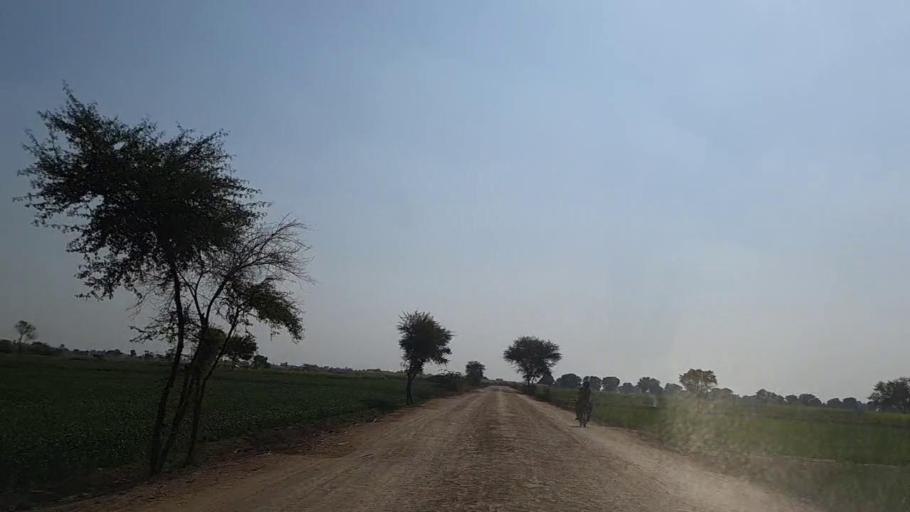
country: PK
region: Sindh
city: Daur
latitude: 26.4727
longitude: 68.2509
